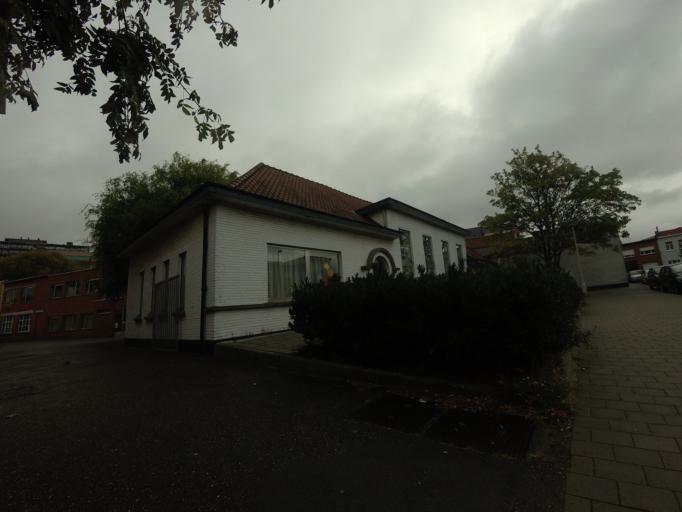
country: BE
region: Flanders
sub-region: Provincie Antwerpen
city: Borsbeek
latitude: 51.2293
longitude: 4.4592
